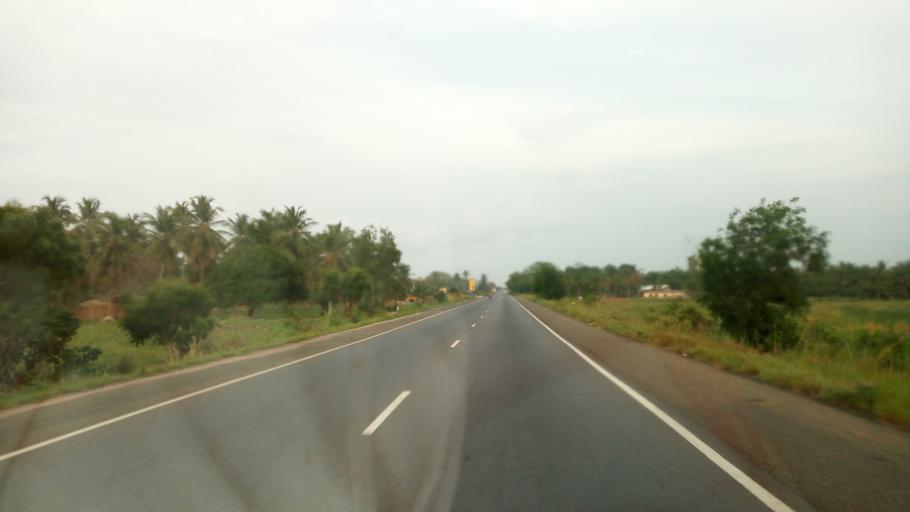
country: TG
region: Maritime
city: Lome
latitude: 6.0947
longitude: 1.0803
